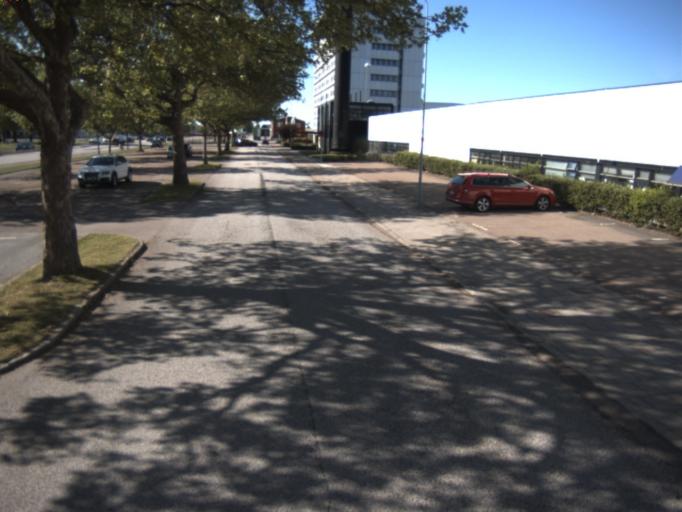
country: SE
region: Skane
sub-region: Helsingborg
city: Rydeback
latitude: 56.0082
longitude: 12.7370
